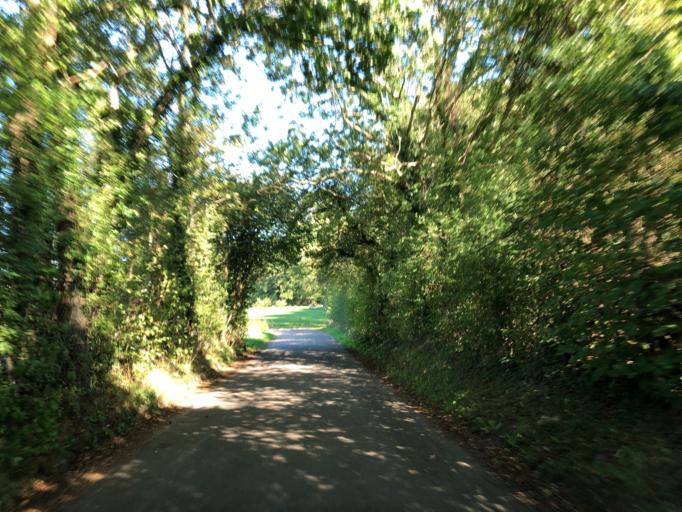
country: DK
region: South Denmark
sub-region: Sonderborg Kommune
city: Dybbol
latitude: 54.9674
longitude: 9.7348
